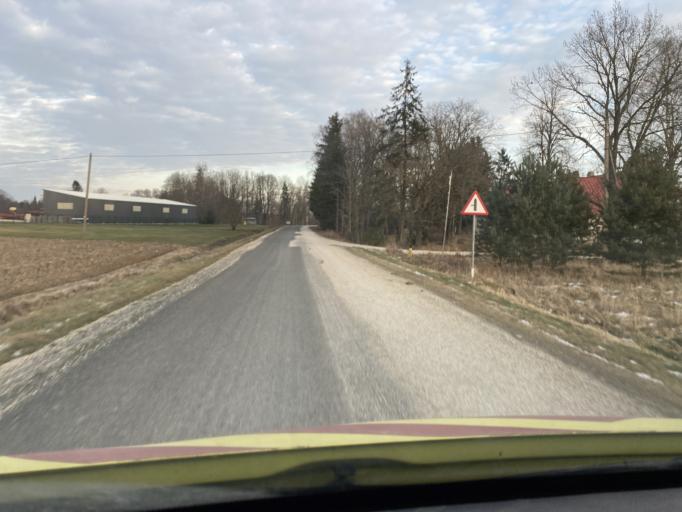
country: EE
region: Jogevamaa
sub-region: Poltsamaa linn
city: Poltsamaa
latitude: 58.5824
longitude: 26.0977
